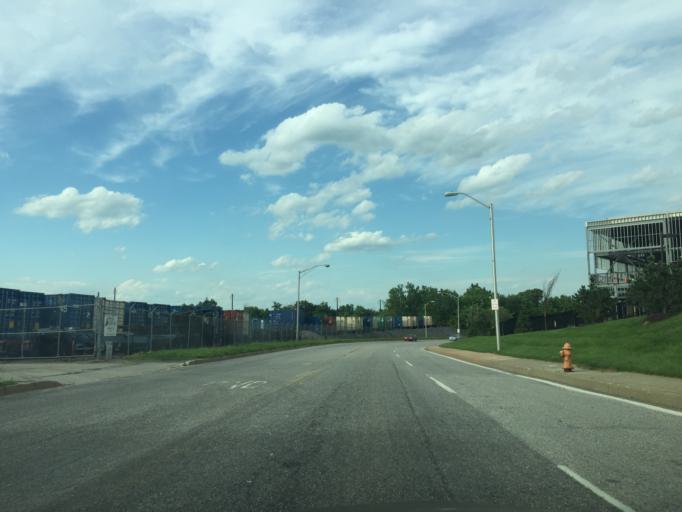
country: US
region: Maryland
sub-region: Baltimore County
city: Rosedale
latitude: 39.2945
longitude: -76.5495
